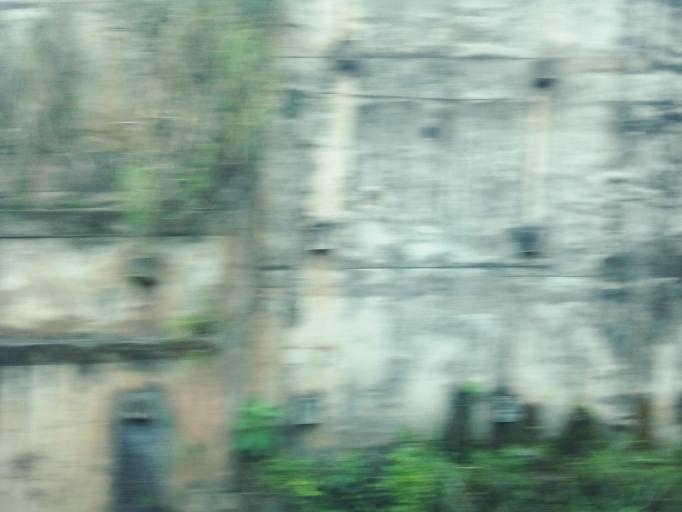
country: BR
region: Minas Gerais
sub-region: Joao Monlevade
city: Joao Monlevade
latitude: -19.8282
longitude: -43.1272
